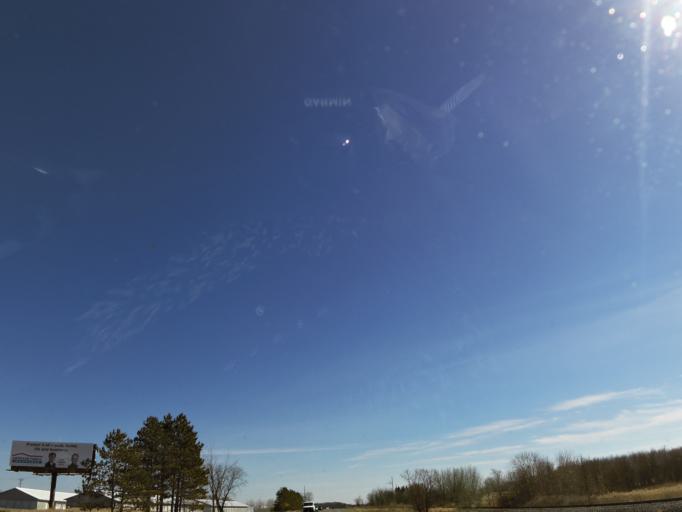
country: US
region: Minnesota
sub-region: Wright County
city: Buffalo
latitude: 45.1419
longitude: -93.8336
